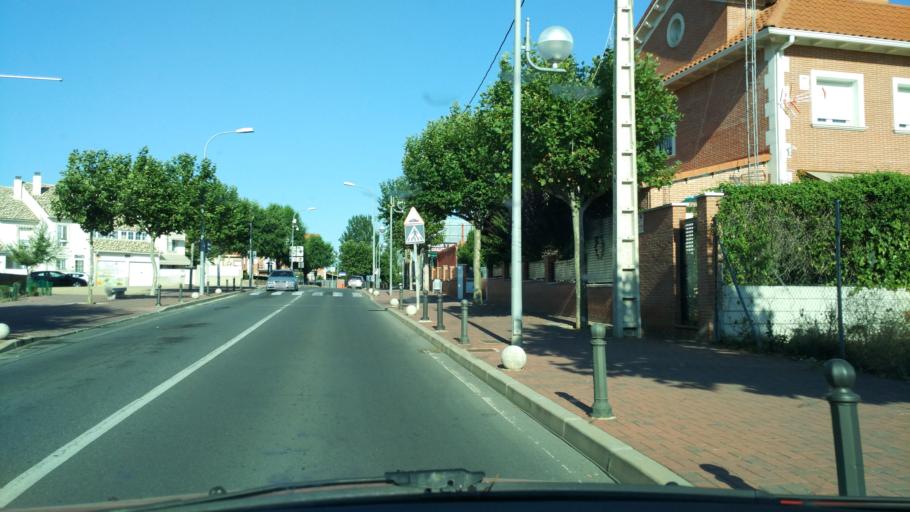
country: ES
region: Madrid
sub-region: Provincia de Madrid
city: Pedrezuela
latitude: 40.7442
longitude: -3.5957
